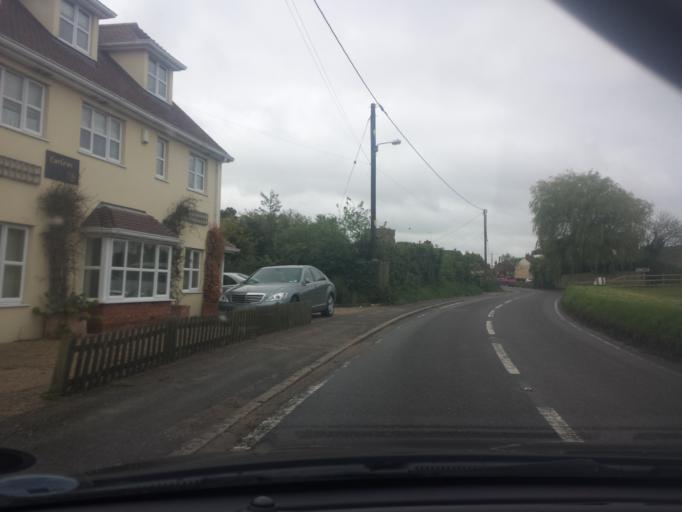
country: GB
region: England
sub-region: Essex
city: Mistley
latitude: 51.9357
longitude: 1.1166
